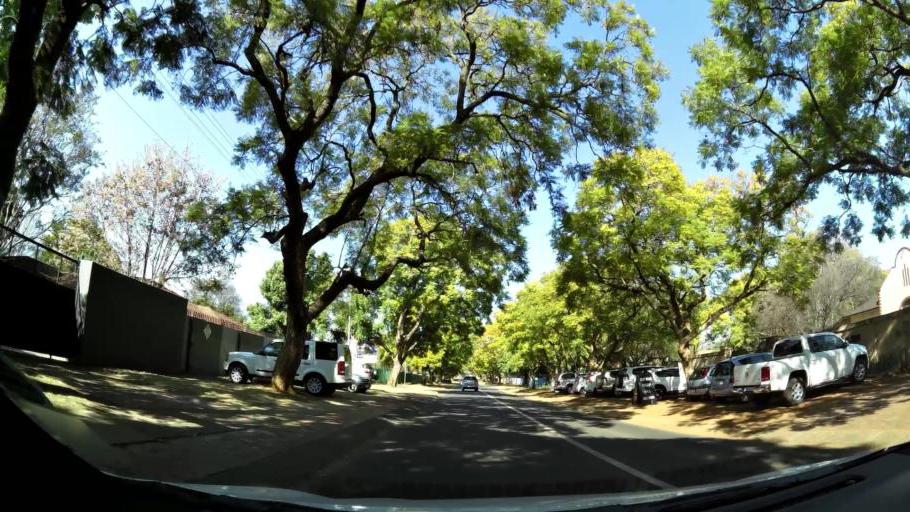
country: ZA
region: Gauteng
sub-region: City of Tshwane Metropolitan Municipality
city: Pretoria
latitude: -25.7647
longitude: 28.2478
